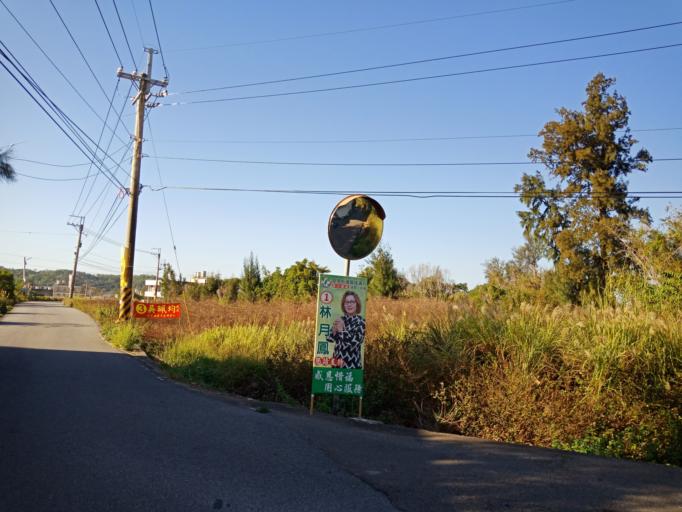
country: TW
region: Taiwan
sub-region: Miaoli
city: Miaoli
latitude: 24.4918
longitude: 120.6956
